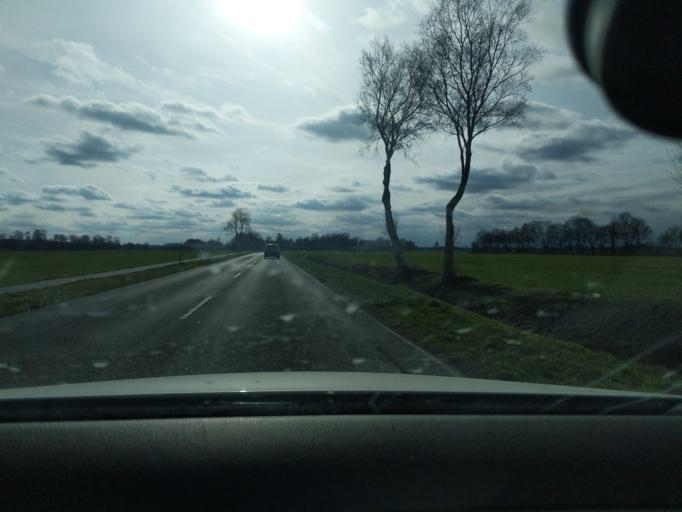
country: DE
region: Lower Saxony
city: Engelschoff
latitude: 53.6608
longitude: 9.3771
